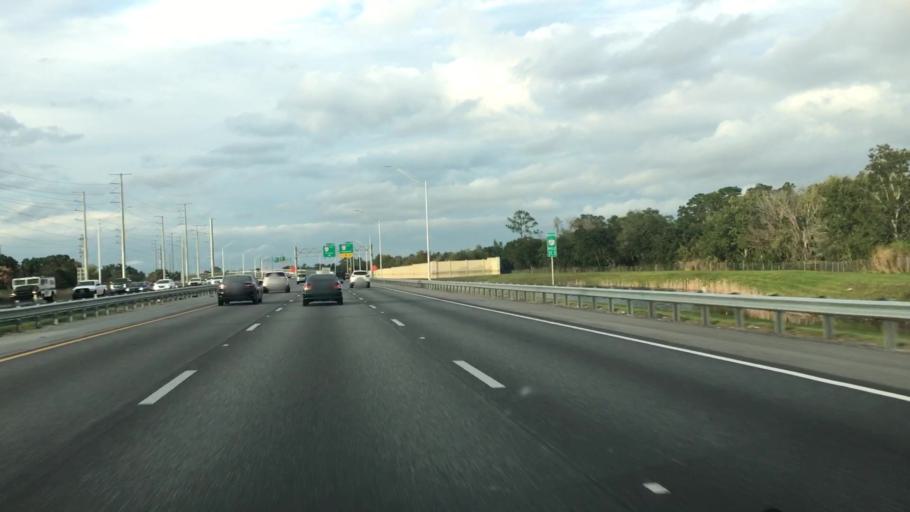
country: US
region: Florida
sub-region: Orange County
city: Union Park
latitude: 28.5328
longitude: -81.2507
